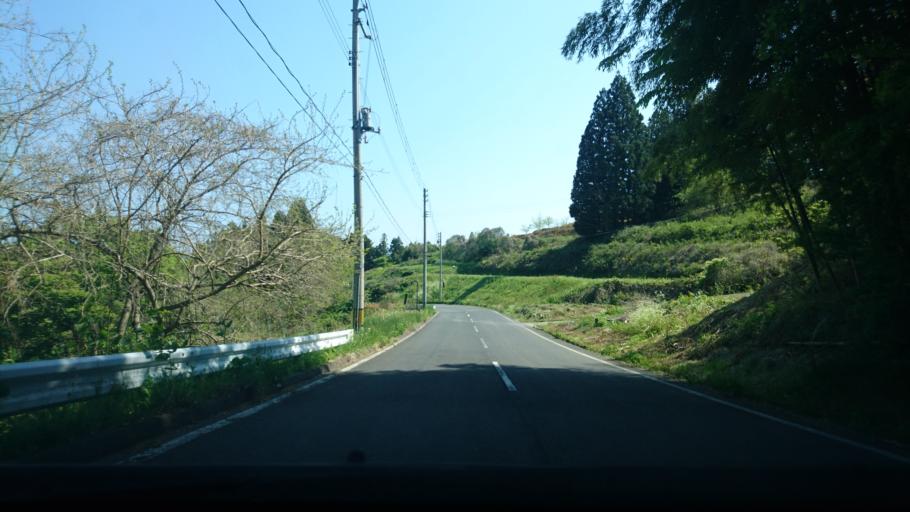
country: JP
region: Iwate
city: Ichinoseki
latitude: 38.9200
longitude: 141.2776
